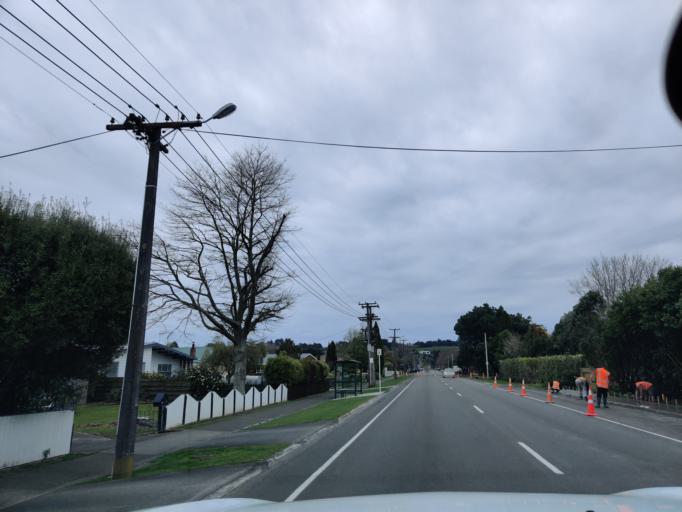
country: NZ
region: Manawatu-Wanganui
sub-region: Palmerston North City
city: Palmerston North
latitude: -40.2871
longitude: 175.7532
